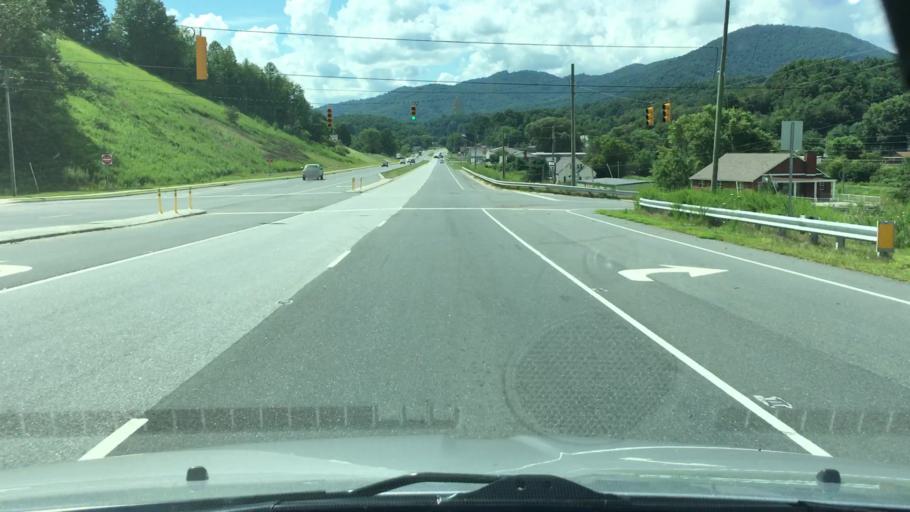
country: US
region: North Carolina
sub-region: Yancey County
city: Burnsville
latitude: 35.9131
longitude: -82.2591
